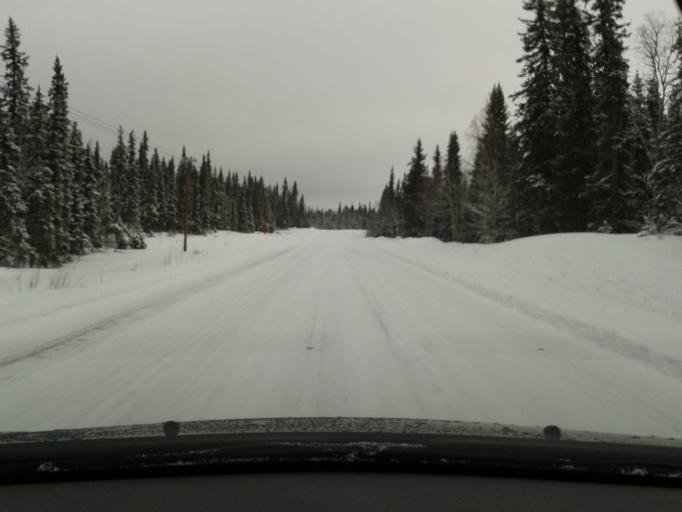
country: SE
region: Vaesterbotten
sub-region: Vilhelmina Kommun
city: Sjoberg
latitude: 65.2347
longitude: 15.8422
